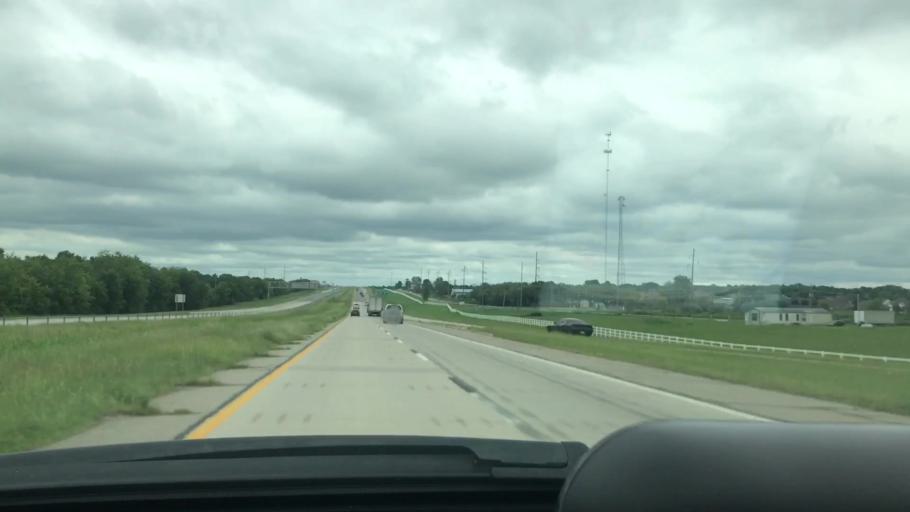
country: US
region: Oklahoma
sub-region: McIntosh County
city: Checotah
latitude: 35.4613
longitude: -95.5426
